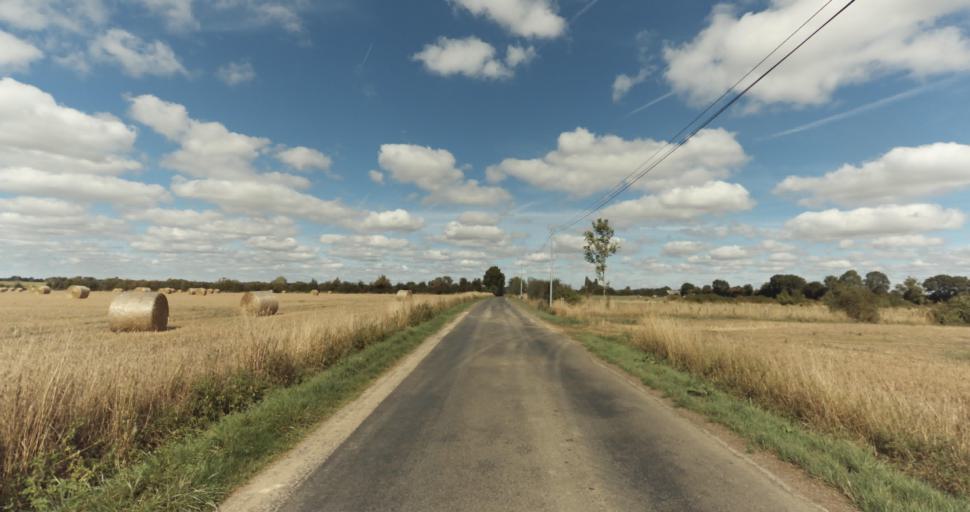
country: FR
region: Lower Normandy
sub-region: Departement de l'Orne
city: Gace
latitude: 48.9051
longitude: 0.3399
